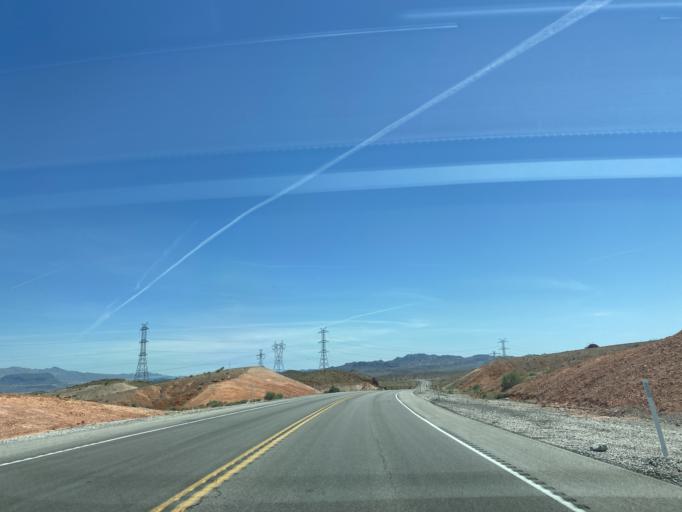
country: US
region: Nevada
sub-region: Clark County
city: Nellis Air Force Base
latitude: 36.1909
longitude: -114.9204
